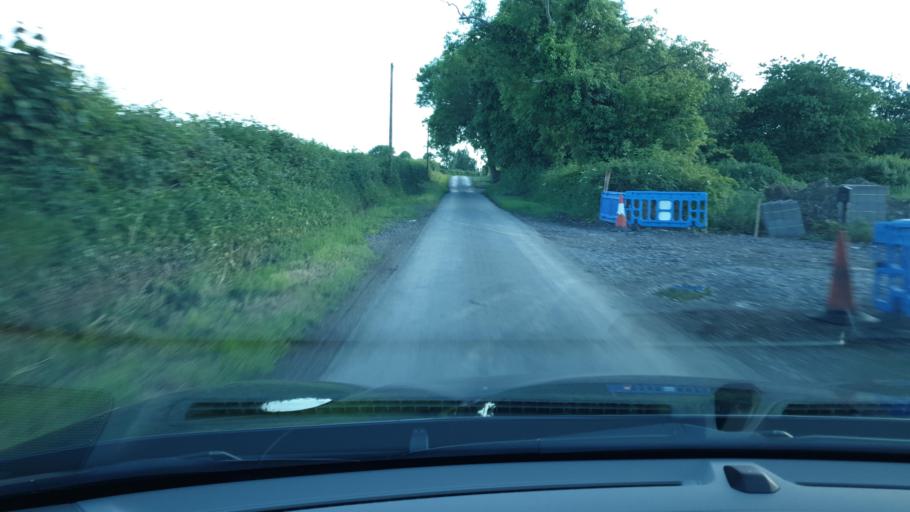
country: IE
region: Leinster
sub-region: An Mhi
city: Ashbourne
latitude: 53.4824
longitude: -6.3501
